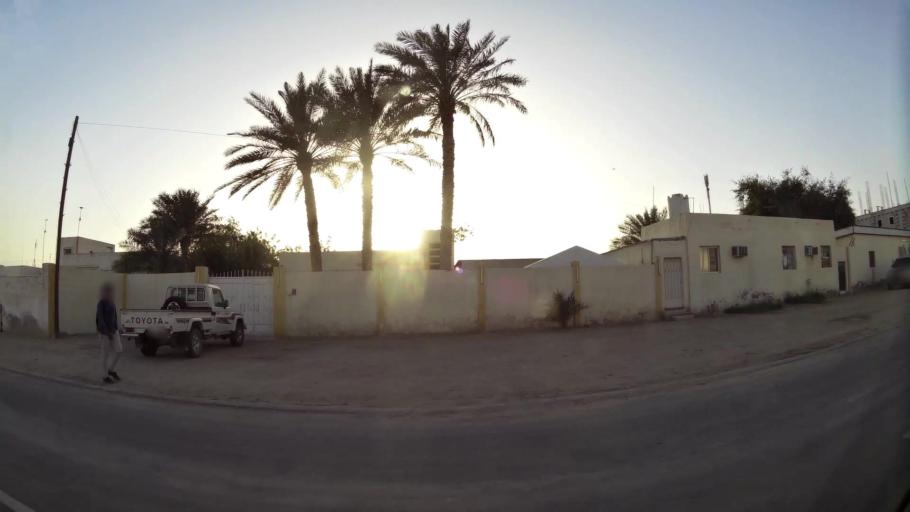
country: QA
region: Baladiyat ar Rayyan
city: Ar Rayyan
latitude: 25.3148
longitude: 51.4578
